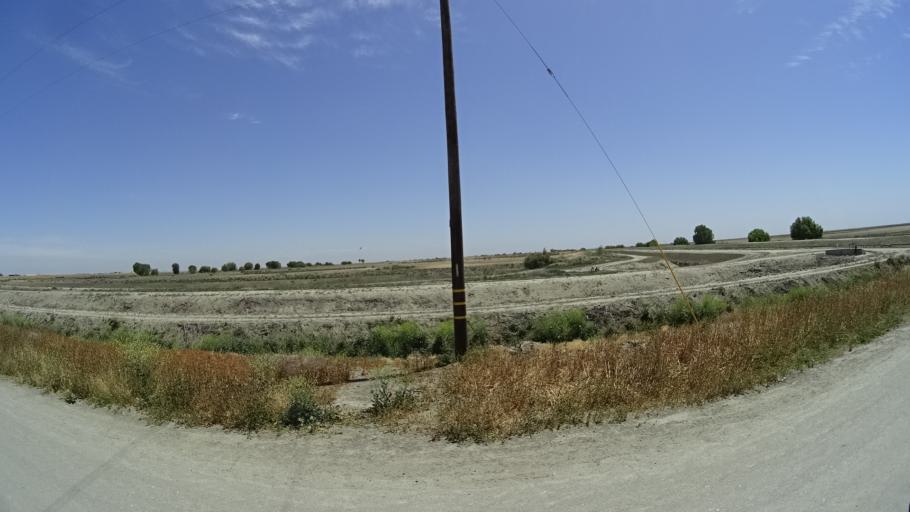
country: US
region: California
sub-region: Kings County
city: Stratford
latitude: 36.1428
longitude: -119.7444
